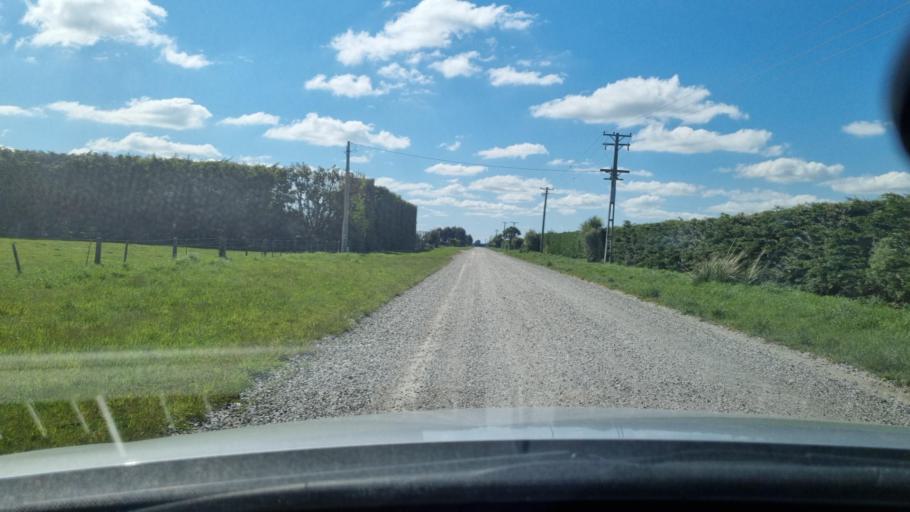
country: NZ
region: Southland
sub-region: Invercargill City
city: Invercargill
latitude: -46.3763
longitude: 168.2985
